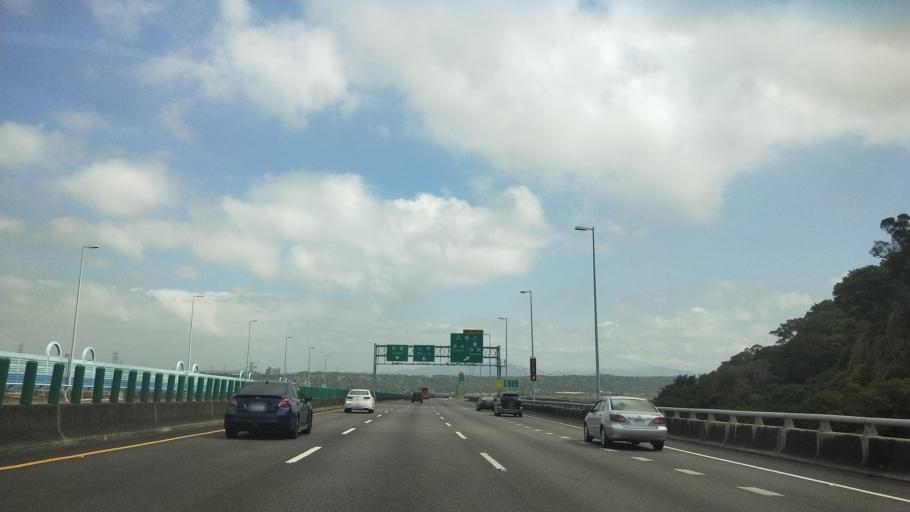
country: TW
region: Taiwan
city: Fengyuan
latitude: 24.3033
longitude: 120.6079
